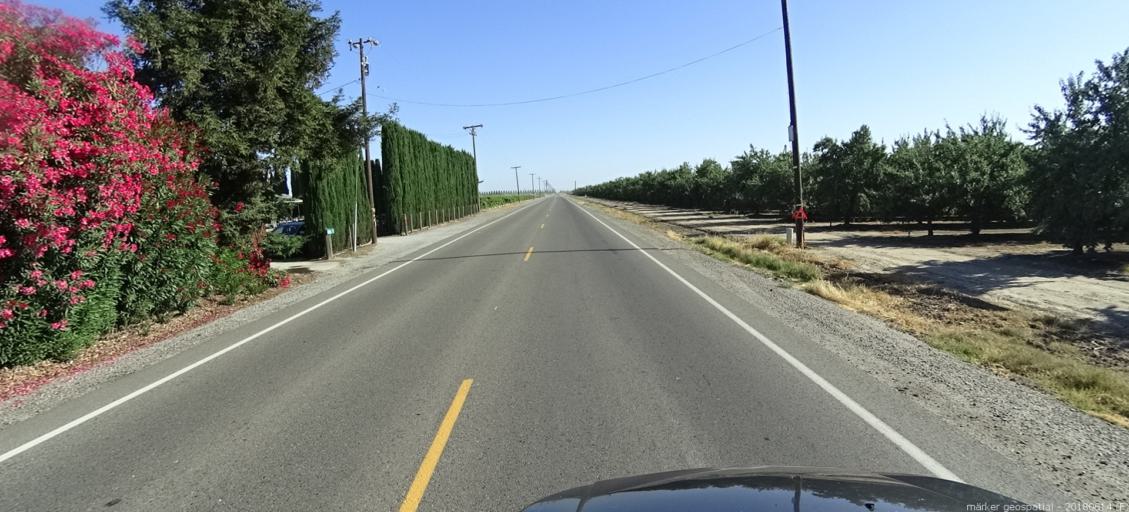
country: US
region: California
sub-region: Madera County
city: Madera
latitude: 36.9558
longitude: -120.1284
